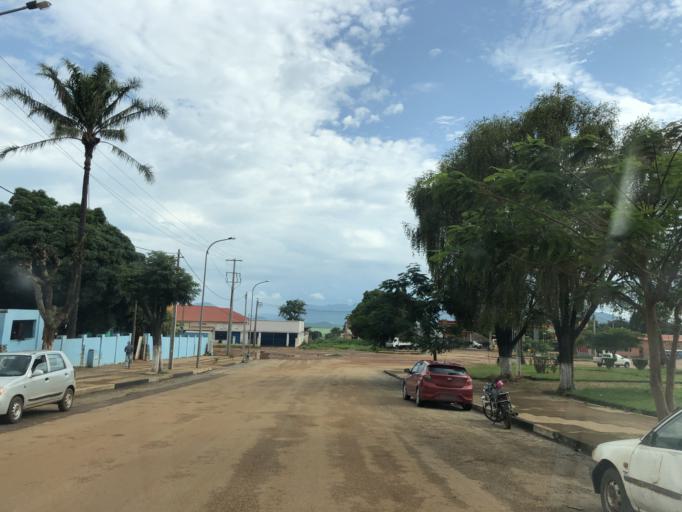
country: AO
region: Cuanza Sul
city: Uacu Cungo
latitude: -11.3626
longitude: 15.1185
